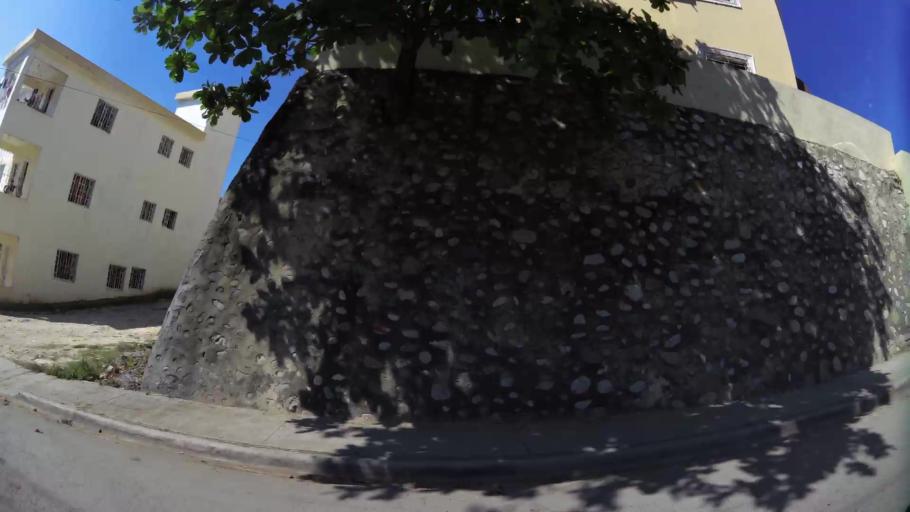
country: DO
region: Santo Domingo
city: Santo Domingo Oeste
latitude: 18.4806
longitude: -70.0013
